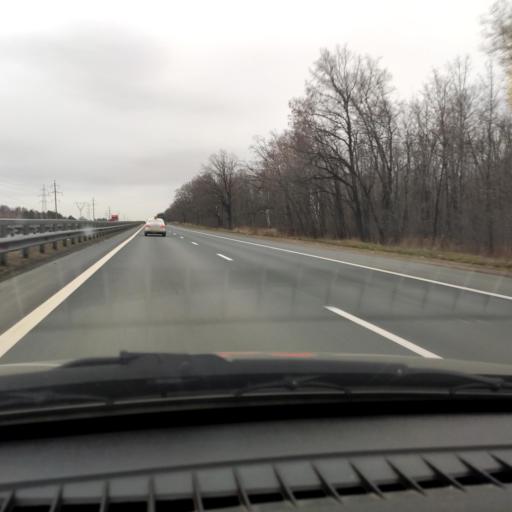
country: RU
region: Samara
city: Pribrezhnyy
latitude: 53.5183
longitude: 49.8153
